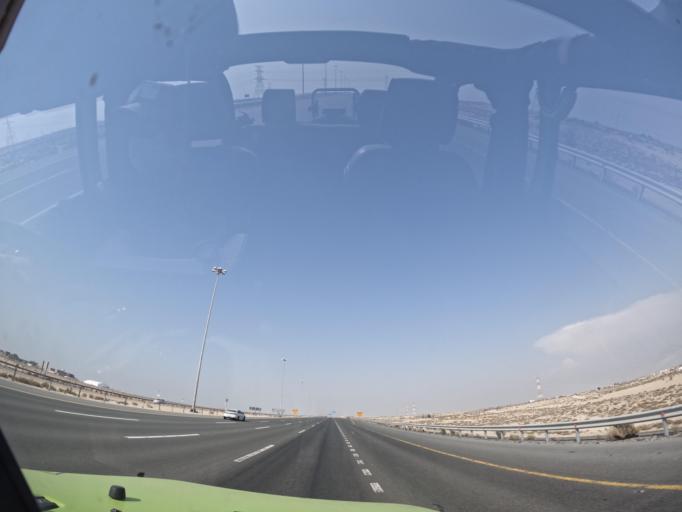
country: AE
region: Abu Dhabi
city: Abu Dhabi
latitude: 24.6542
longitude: 54.7973
